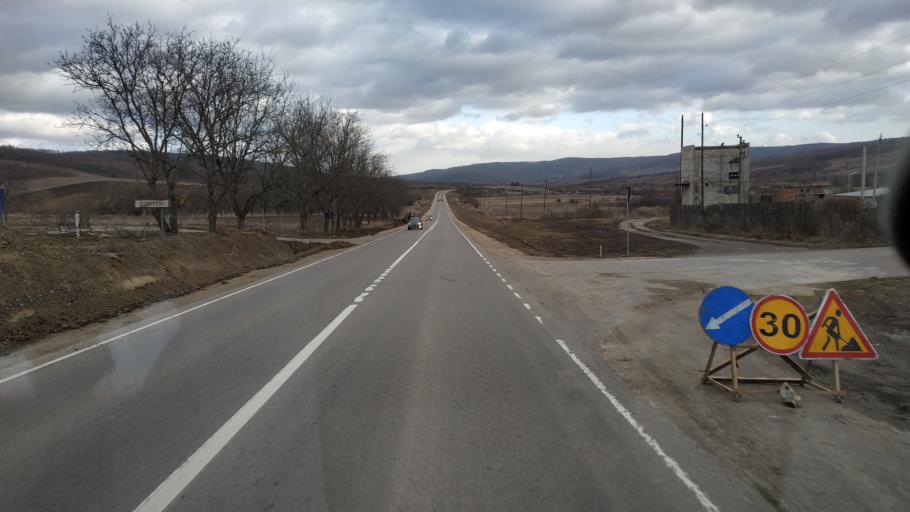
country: MD
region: Calarasi
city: Calarasi
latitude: 47.2748
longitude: 28.2180
